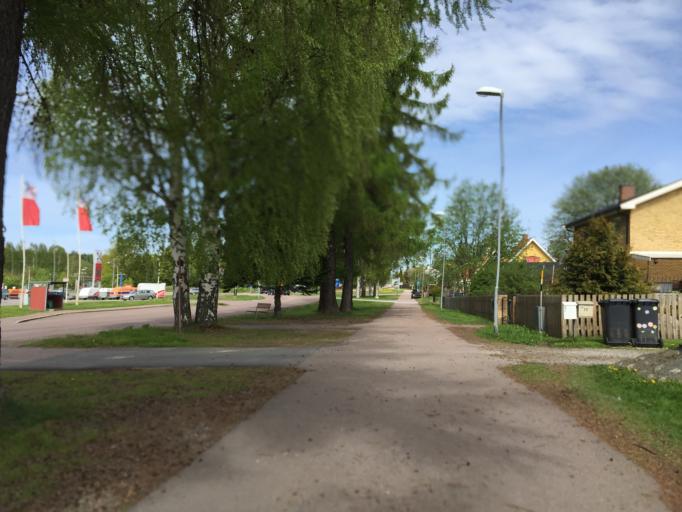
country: SE
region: Dalarna
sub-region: Ludvika Kommun
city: Ludvika
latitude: 60.1306
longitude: 15.1791
